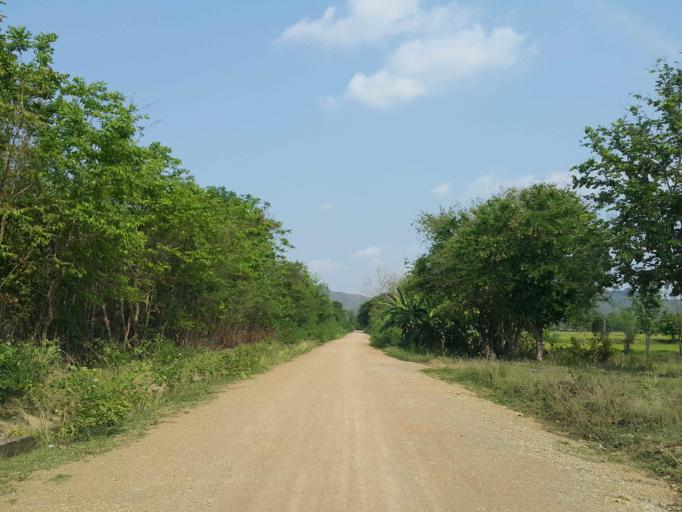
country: TH
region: Sukhothai
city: Thung Saliam
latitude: 17.3321
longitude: 99.4354
